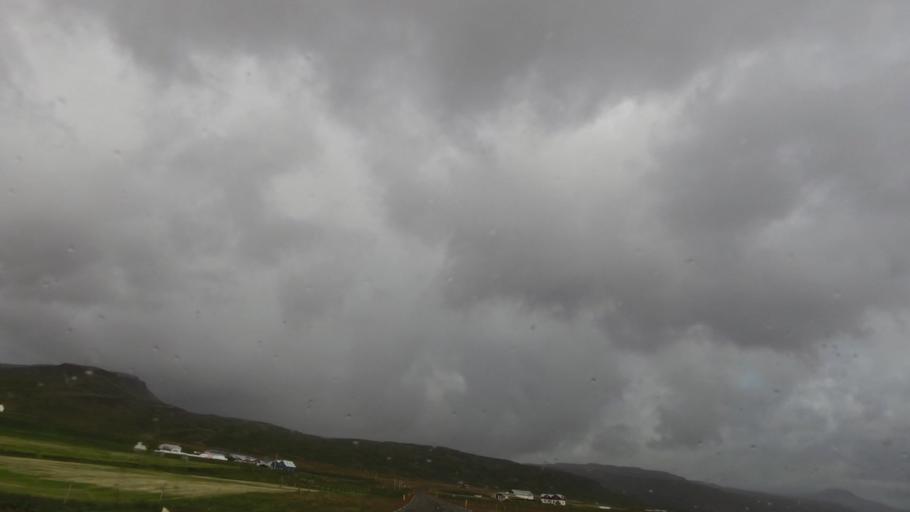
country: IS
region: Westfjords
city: Isafjoerdur
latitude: 65.5234
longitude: -23.1894
